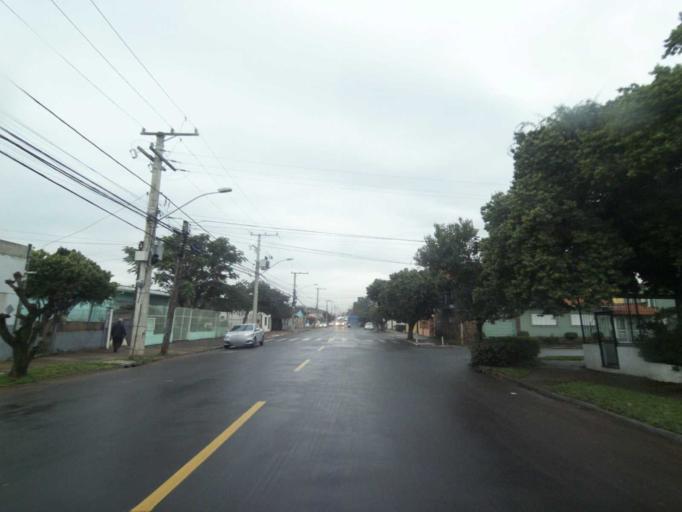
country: BR
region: Rio Grande do Sul
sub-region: Sao Leopoldo
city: Sao Leopoldo
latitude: -29.7710
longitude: -51.1553
